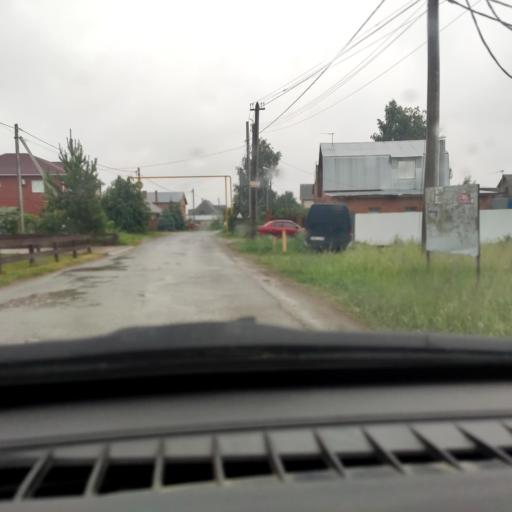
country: RU
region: Samara
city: Tol'yatti
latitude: 53.5651
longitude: 49.3813
